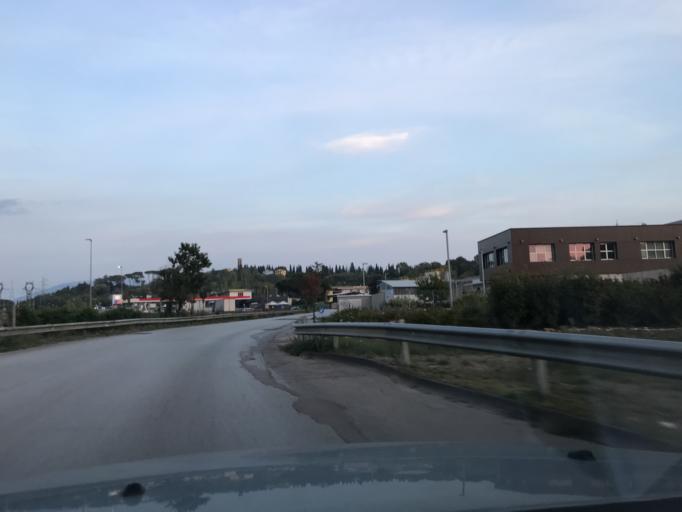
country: IT
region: Umbria
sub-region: Provincia di Perugia
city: Via Lippia
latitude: 43.0881
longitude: 12.4621
